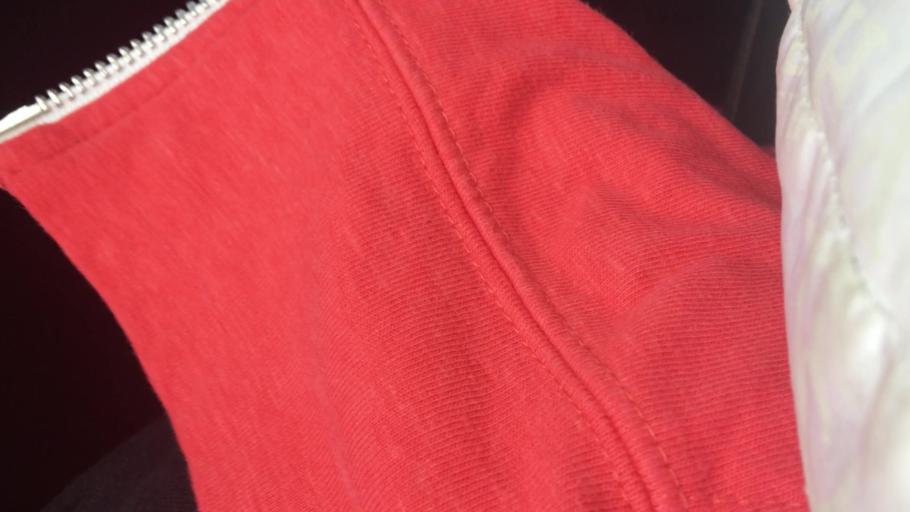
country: IT
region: Molise
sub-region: Provincia di Isernia
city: Carovilli
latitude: 41.7338
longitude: 14.2630
